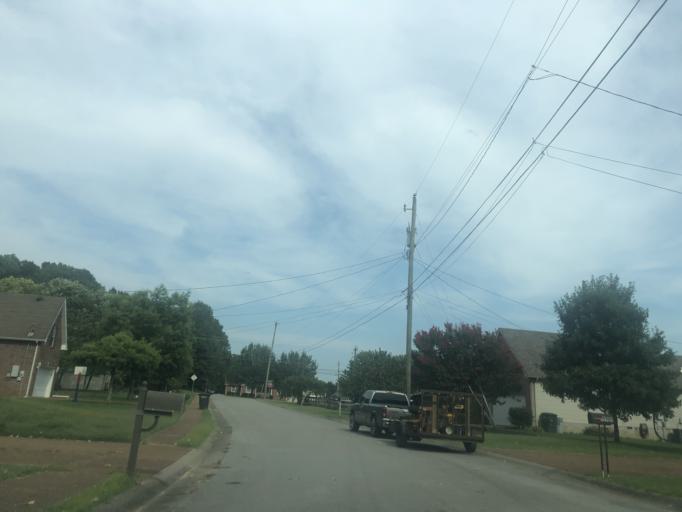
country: US
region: Tennessee
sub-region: Wilson County
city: Green Hill
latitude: 36.1811
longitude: -86.5835
